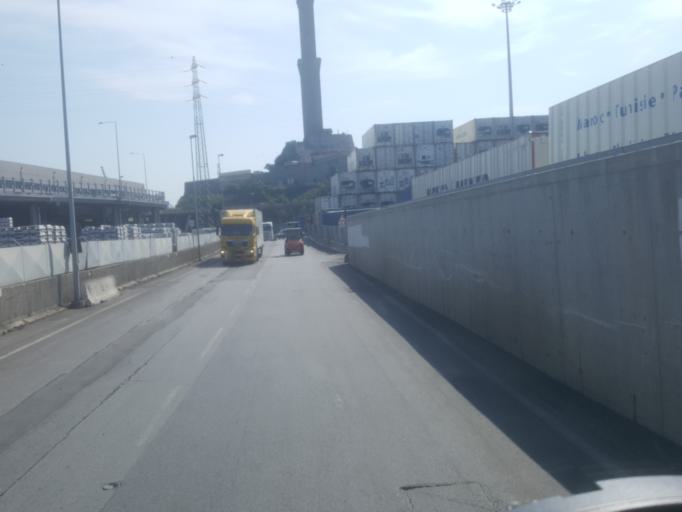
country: IT
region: Liguria
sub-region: Provincia di Genova
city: San Teodoro
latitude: 44.4054
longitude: 8.9008
